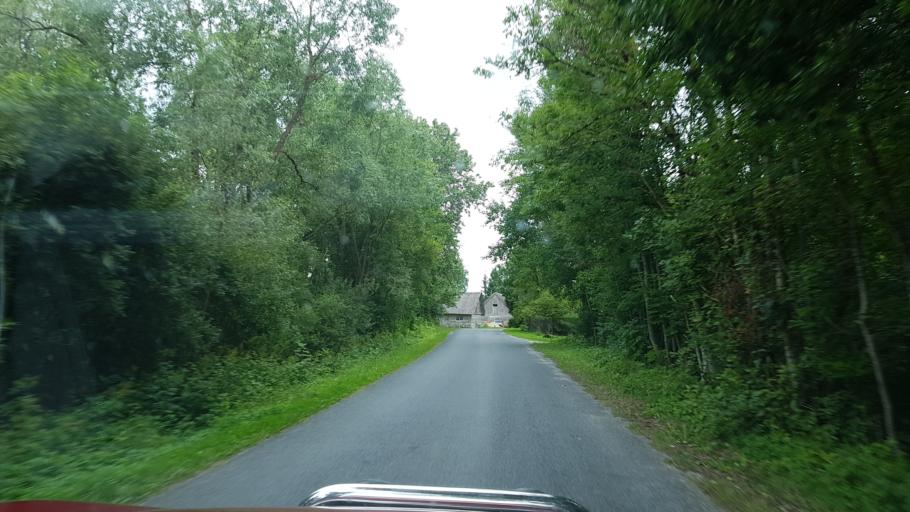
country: EE
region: Laeaene
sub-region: Ridala Parish
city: Uuemoisa
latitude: 58.8034
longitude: 23.6662
